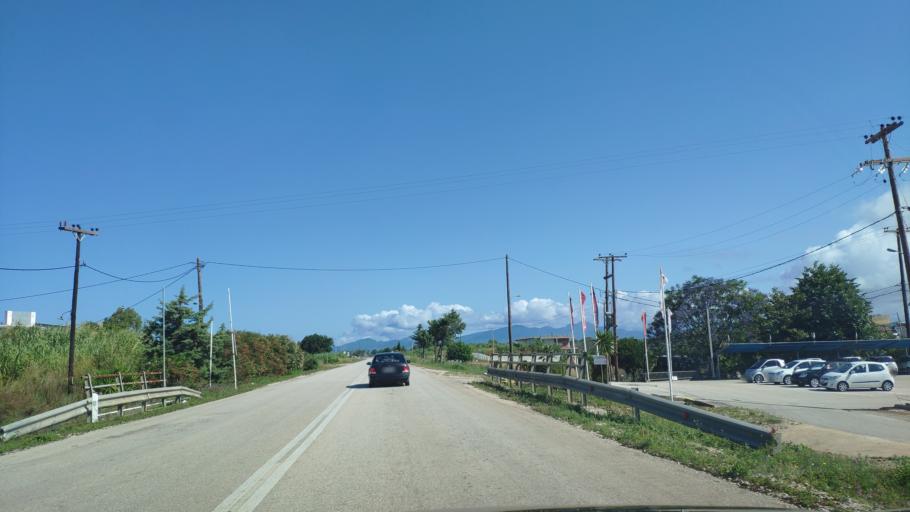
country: GR
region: Epirus
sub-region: Nomos Prevezis
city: Preveza
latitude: 38.9713
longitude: 20.7223
